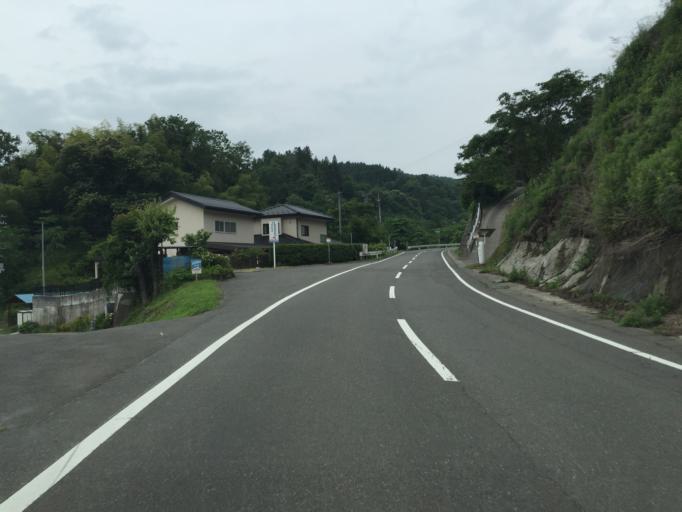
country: JP
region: Fukushima
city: Fukushima-shi
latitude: 37.6536
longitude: 140.5893
